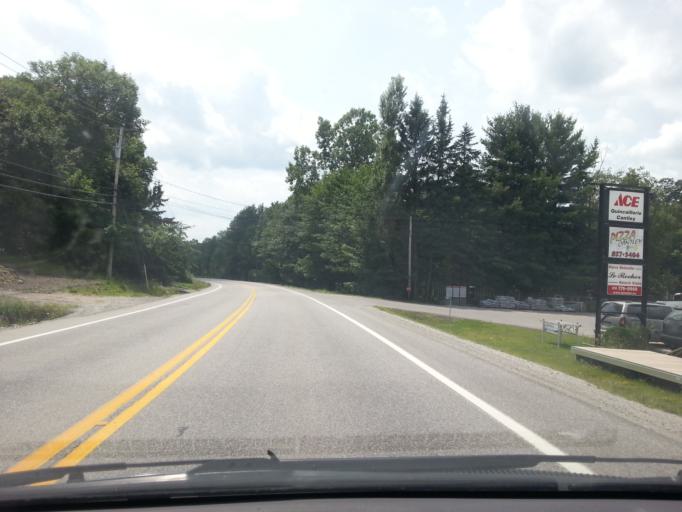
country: CA
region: Quebec
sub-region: Outaouais
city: Gatineau
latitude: 45.5282
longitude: -75.7757
